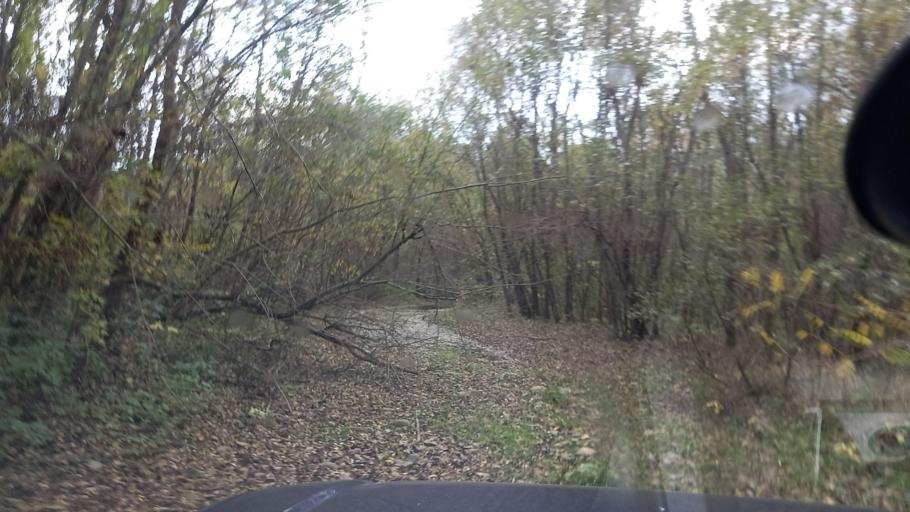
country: RU
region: Krasnodarskiy
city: Shedok
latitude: 44.1691
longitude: 40.8480
